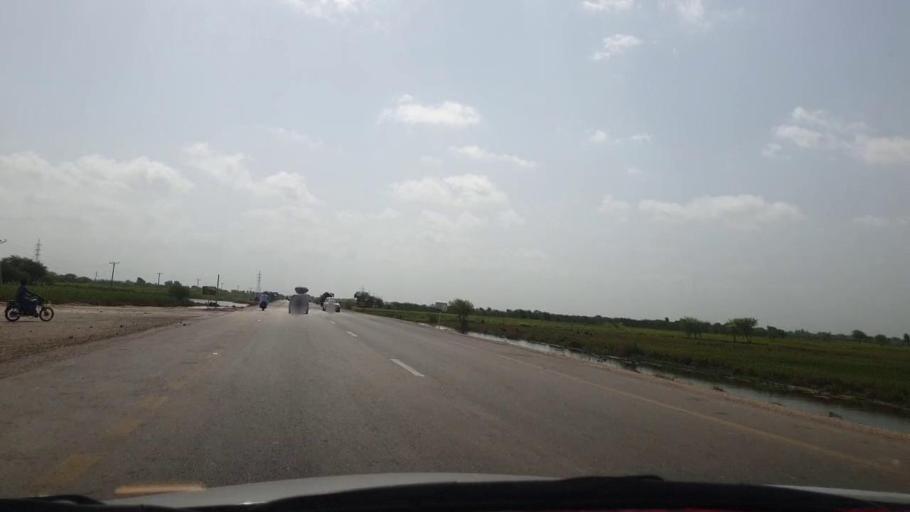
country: PK
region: Sindh
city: Talhar
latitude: 24.9299
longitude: 68.7142
